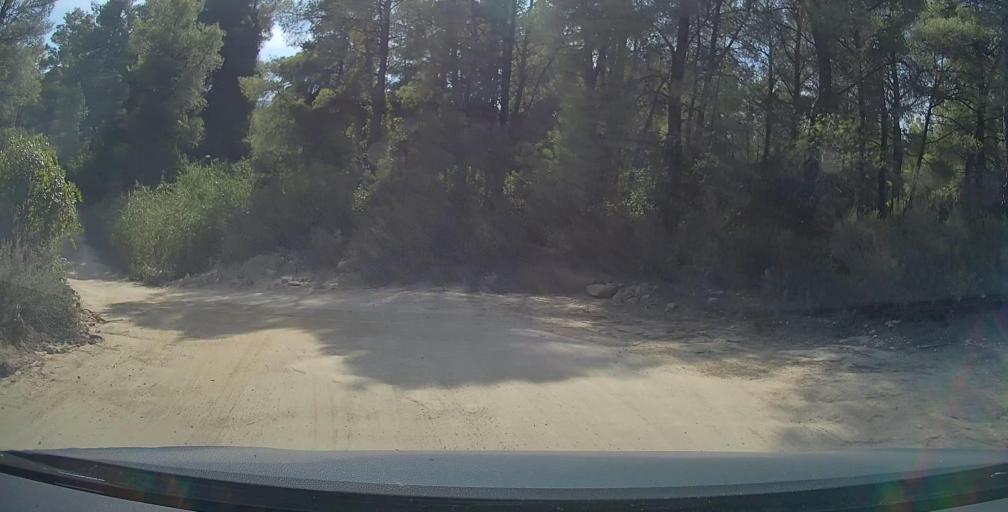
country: GR
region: Central Macedonia
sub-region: Nomos Chalkidikis
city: Sarti
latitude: 40.1296
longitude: 23.9529
